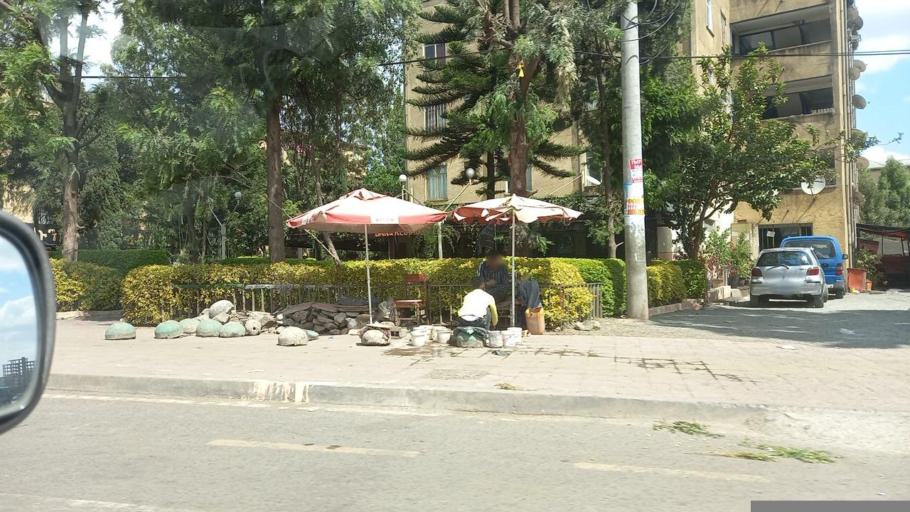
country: ET
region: Adis Abeba
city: Addis Ababa
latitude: 8.9567
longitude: 38.7130
